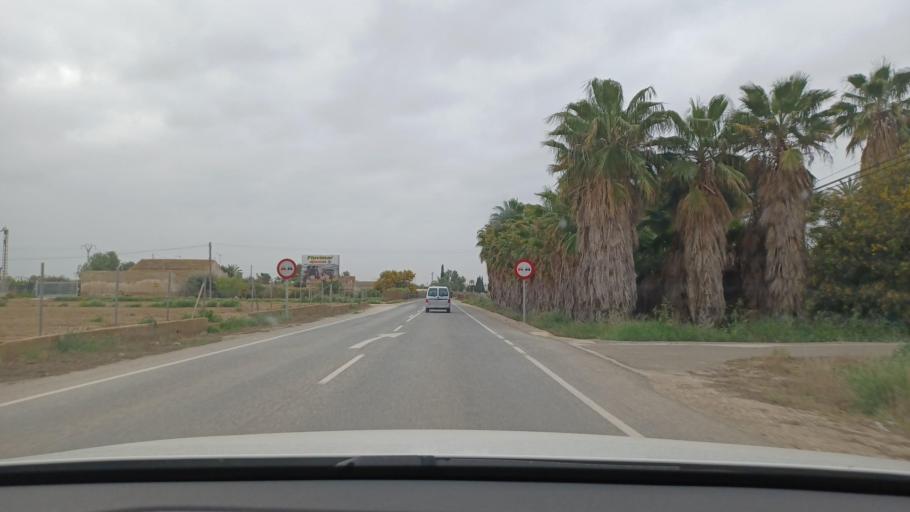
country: ES
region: Valencia
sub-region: Provincia de Alicante
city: Elche
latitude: 38.2288
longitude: -0.7181
